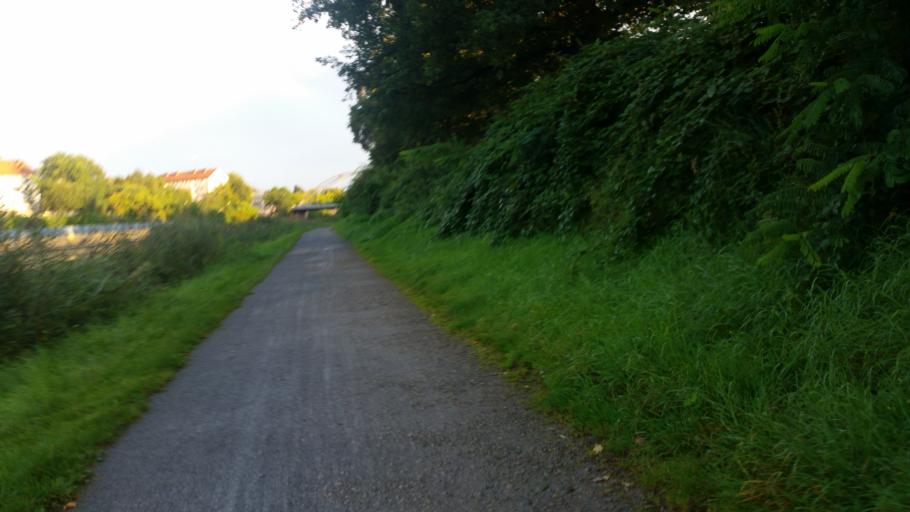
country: DE
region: Lower Saxony
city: Isernhagen Farster Bauerschaft
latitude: 52.4022
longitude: 9.8176
